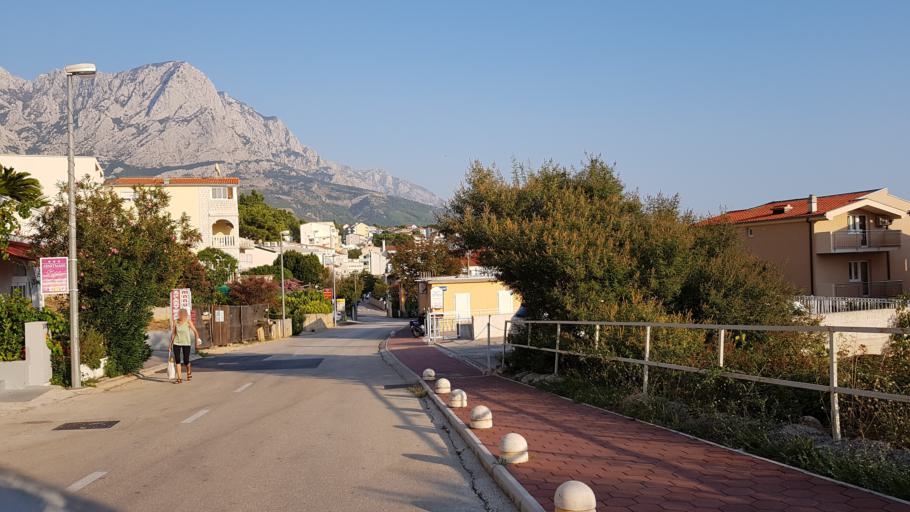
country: HR
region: Splitsko-Dalmatinska
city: Baska Voda
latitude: 43.3600
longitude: 16.9482
